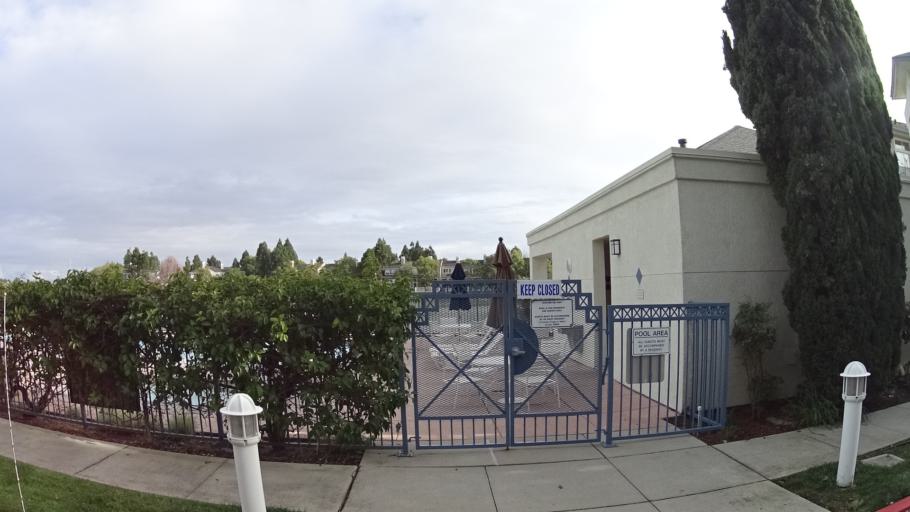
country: US
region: California
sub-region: San Mateo County
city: Redwood Shores
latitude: 37.5383
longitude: -122.2408
